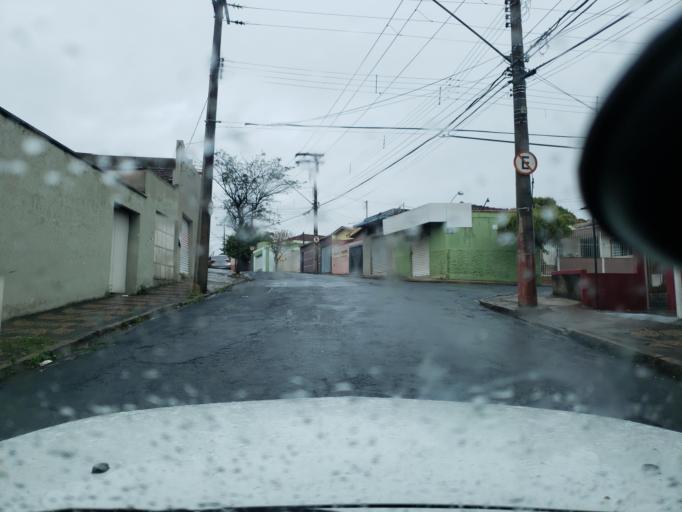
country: BR
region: Sao Paulo
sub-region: Moji-Guacu
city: Mogi-Gaucu
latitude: -22.3751
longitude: -46.9378
